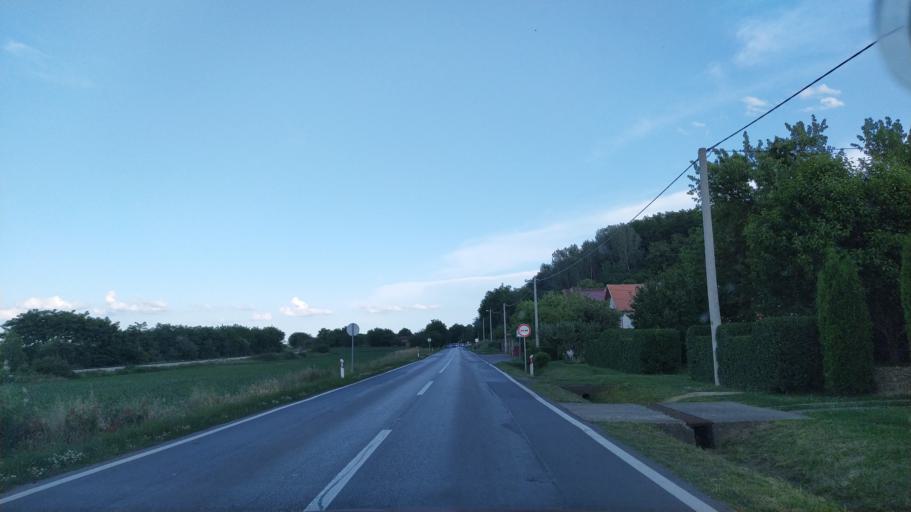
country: HR
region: Virovitick-Podravska
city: Slatina
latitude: 45.7453
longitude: 17.6003
